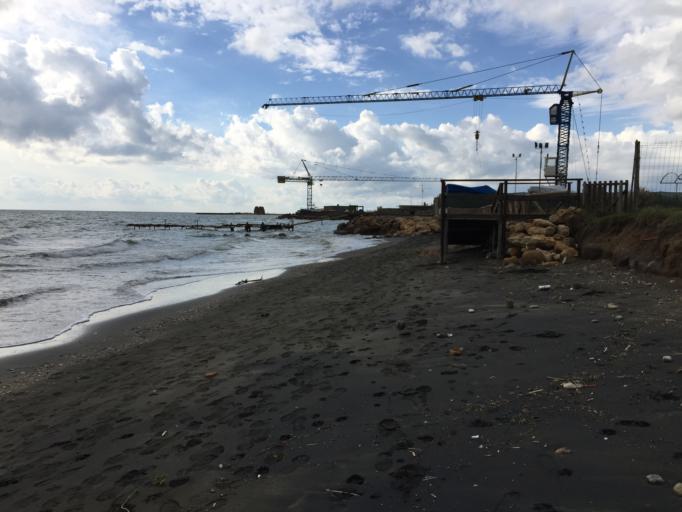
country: IT
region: Latium
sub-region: Citta metropolitana di Roma Capitale
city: Ladispoli
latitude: 41.9546
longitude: 12.0571
